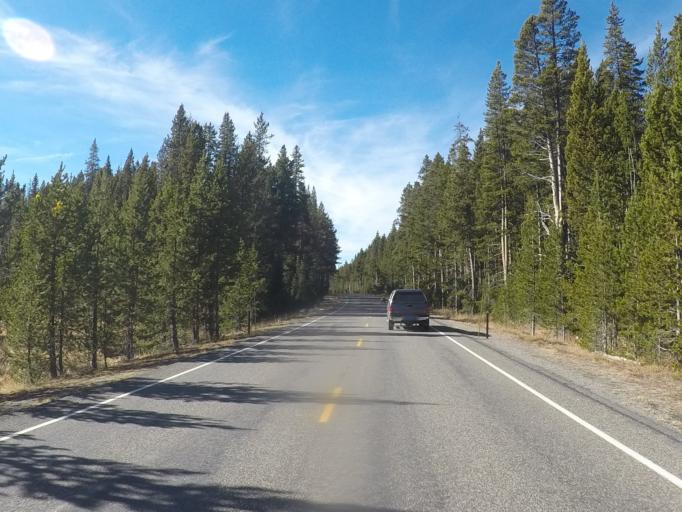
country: US
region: Montana
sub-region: Gallatin County
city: West Yellowstone
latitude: 44.4572
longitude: -110.4895
